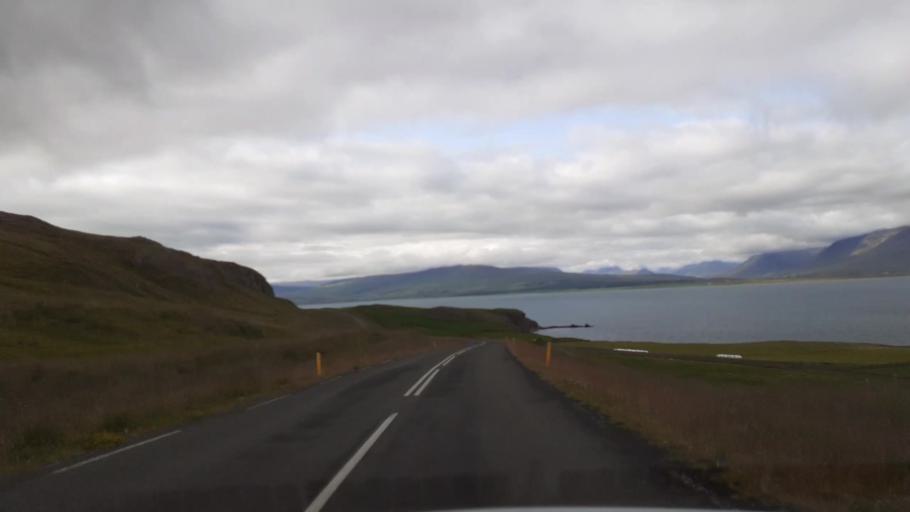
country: IS
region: Northeast
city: Akureyri
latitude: 65.8143
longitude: -18.0497
